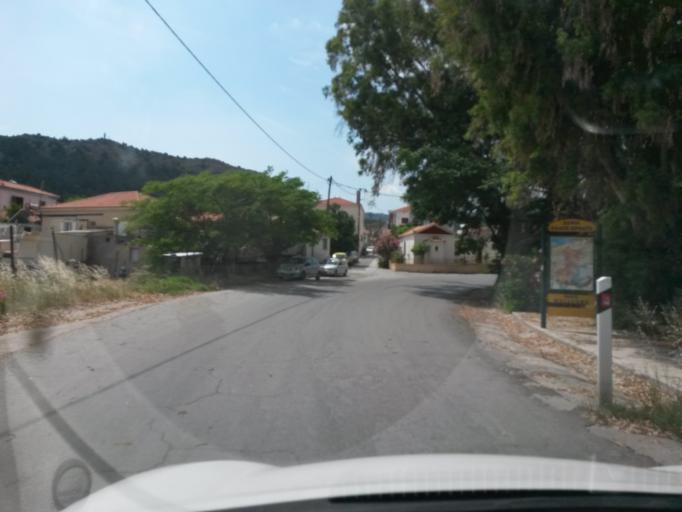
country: GR
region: North Aegean
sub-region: Nomos Lesvou
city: Kalloni
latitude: 39.2414
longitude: 26.2022
